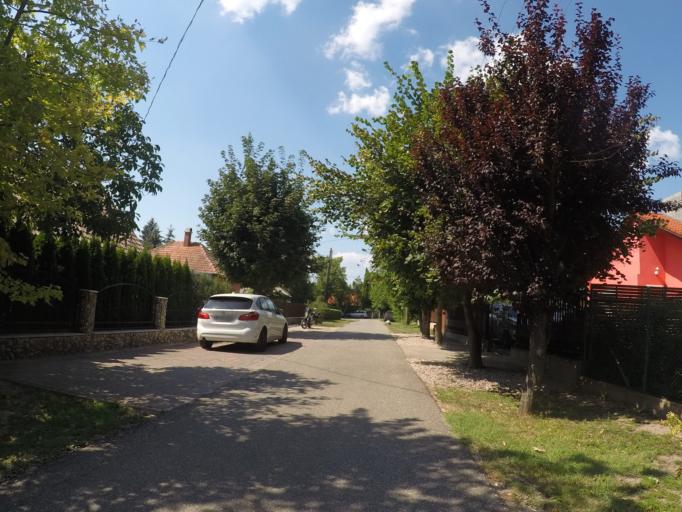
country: HU
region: Somogy
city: Balatonszabadi
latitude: 46.9320
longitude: 18.1217
